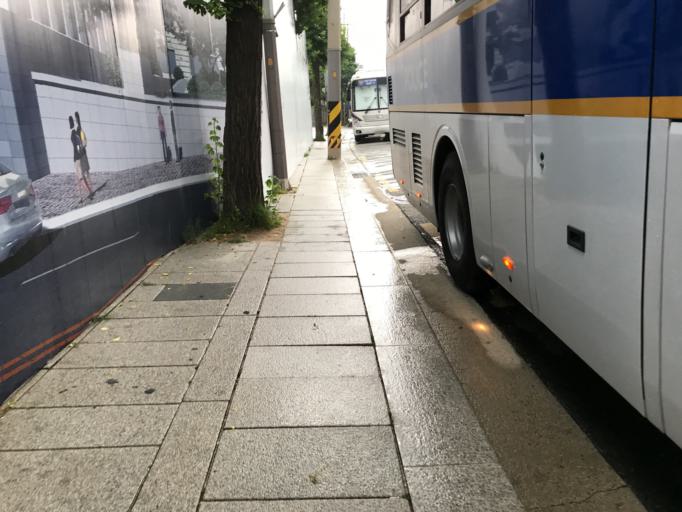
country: KR
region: Seoul
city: Seoul
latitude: 37.5777
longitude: 126.9857
